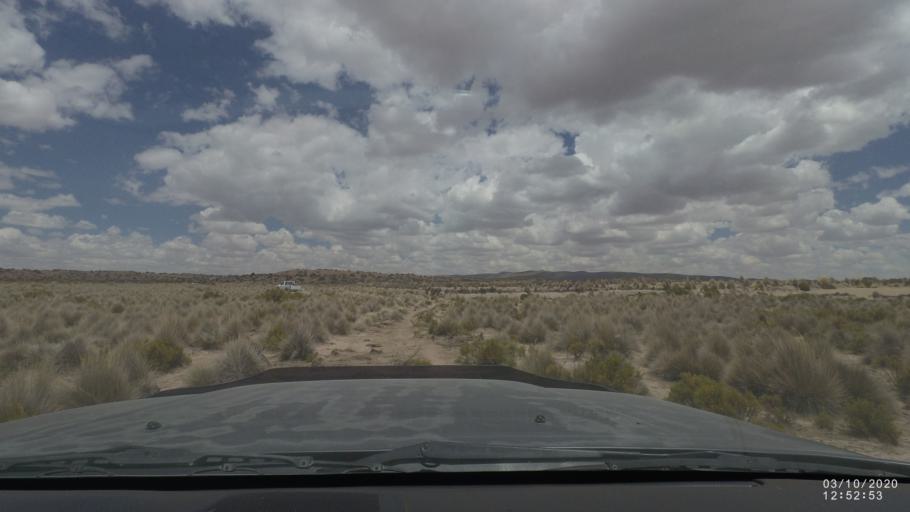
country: BO
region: Oruro
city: Poopo
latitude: -18.6886
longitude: -67.5359
